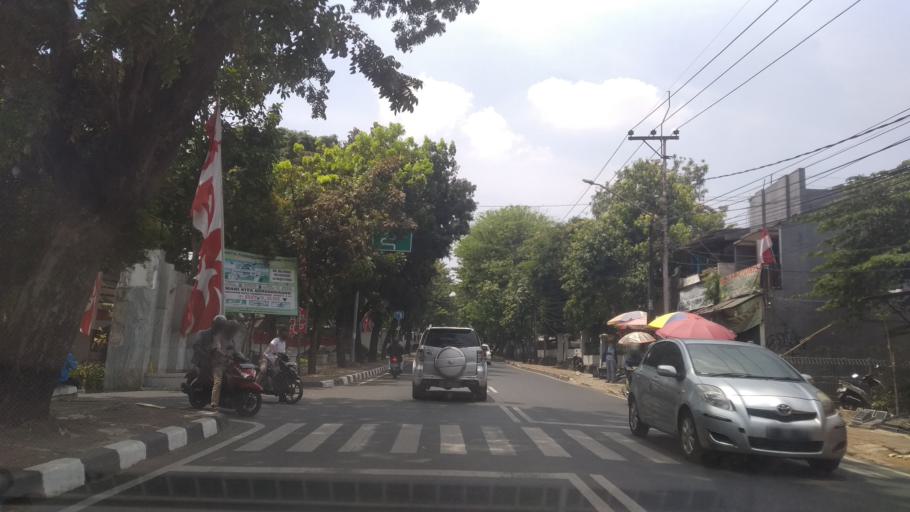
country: ID
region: Banten
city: South Tangerang
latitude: -6.2530
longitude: 106.7716
